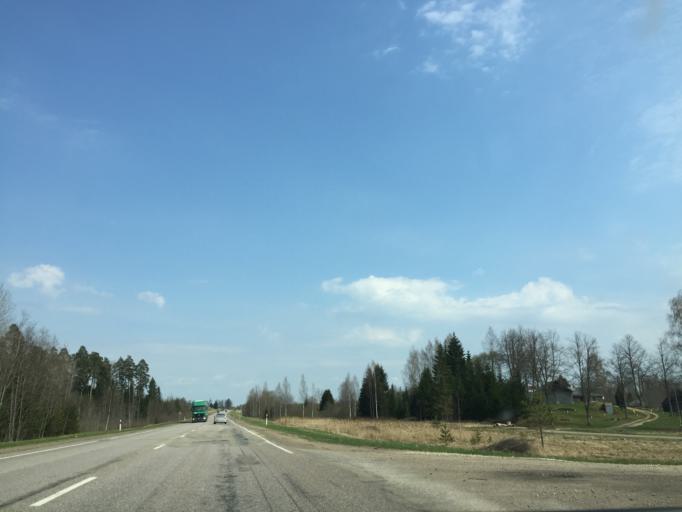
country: LV
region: Apes Novads
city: Ape
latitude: 57.4867
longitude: 26.5603
